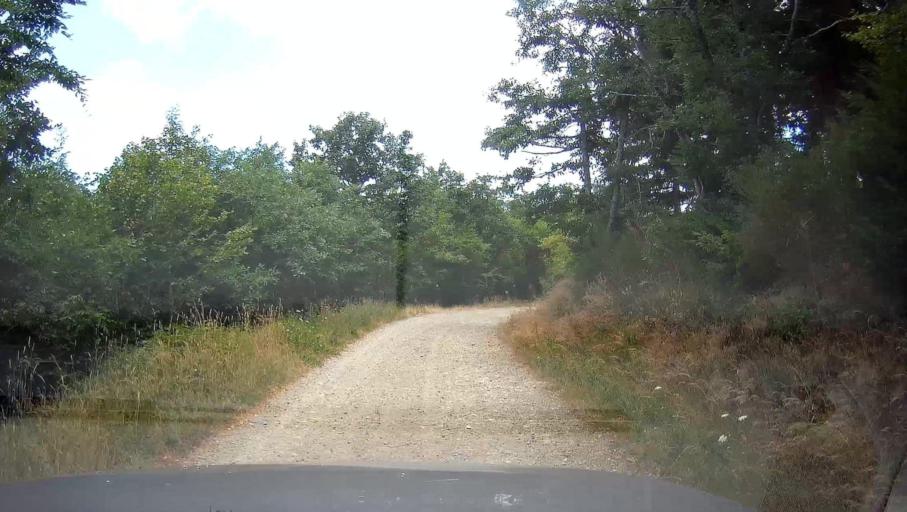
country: FR
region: Rhone-Alpes
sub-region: Departement du Rhone
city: Le Perreon
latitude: 46.0254
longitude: 4.5483
